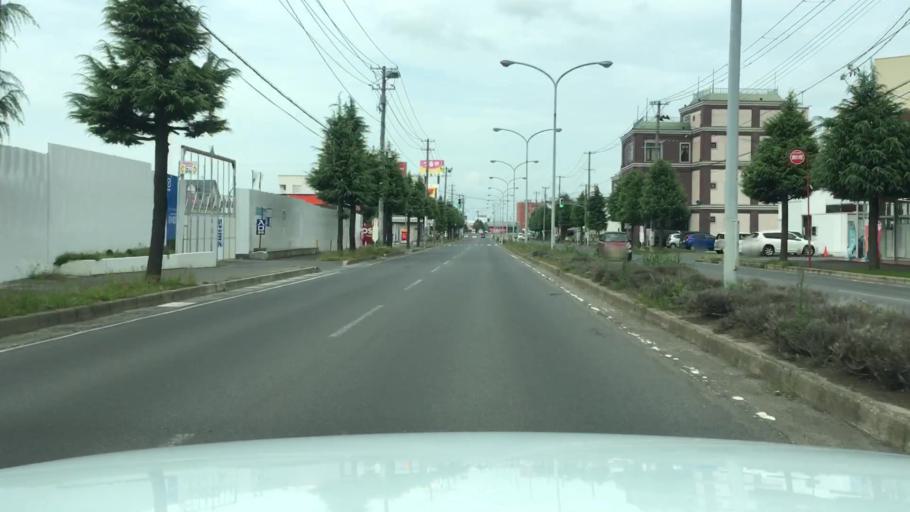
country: JP
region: Aomori
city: Hirosaki
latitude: 40.6072
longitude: 140.4792
